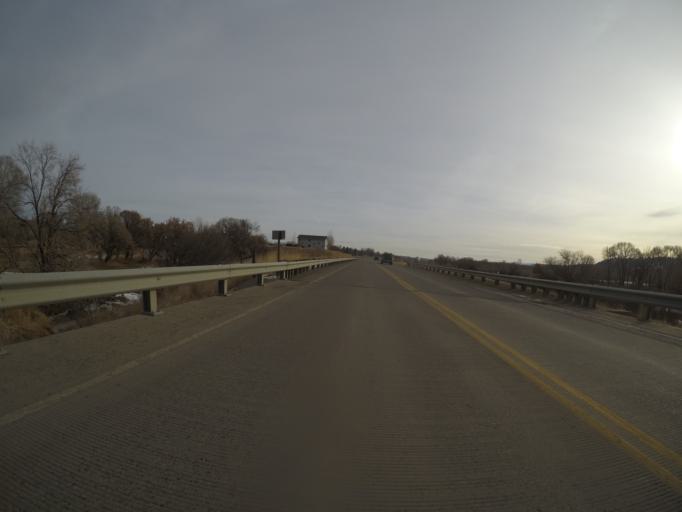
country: US
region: Montana
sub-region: Stillwater County
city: Columbus
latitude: 45.6410
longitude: -109.2714
